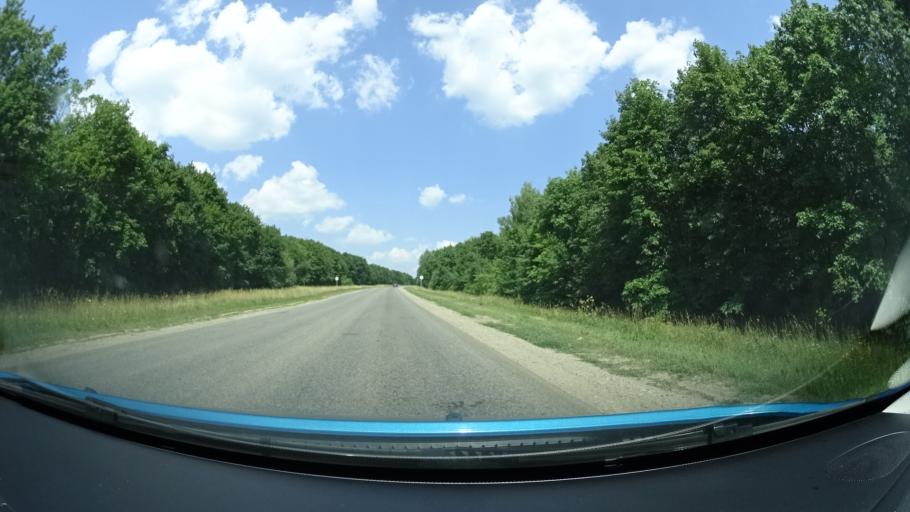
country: RU
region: Bashkortostan
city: Oktyabr'skiy
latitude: 54.4659
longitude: 53.5749
